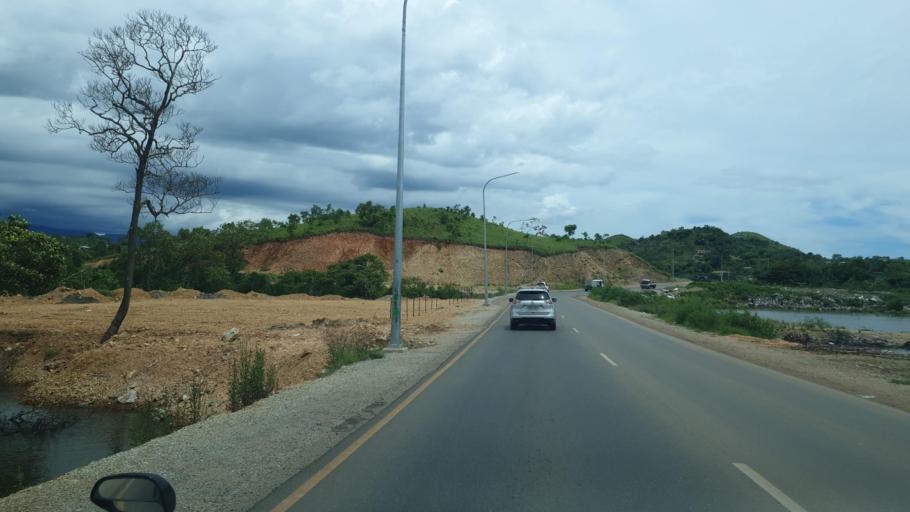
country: PG
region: National Capital
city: Port Moresby
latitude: -9.5061
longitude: 147.2385
